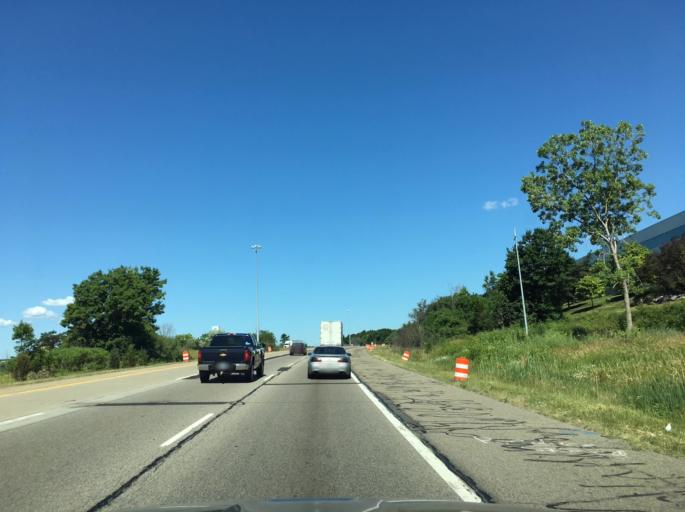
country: US
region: Michigan
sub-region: Oakland County
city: Auburn Hills
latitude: 42.6962
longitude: -83.2711
